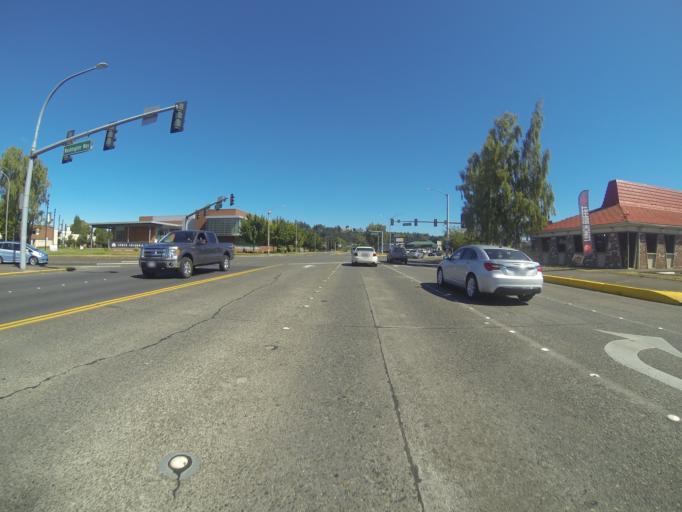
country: US
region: Washington
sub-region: Cowlitz County
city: Longview
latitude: 46.1404
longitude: -122.9359
